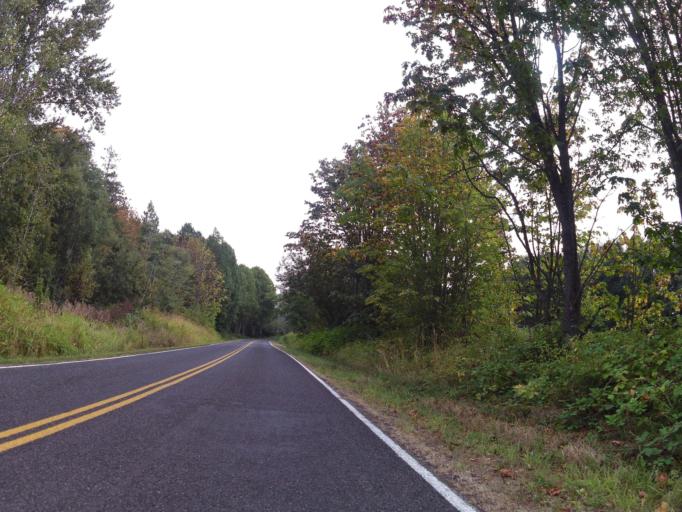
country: US
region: Washington
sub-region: Whatcom County
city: Ferndale
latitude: 48.8066
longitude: -122.6661
